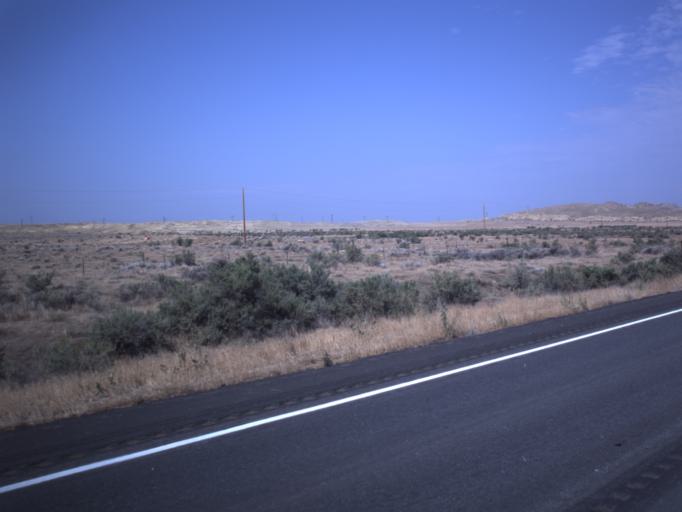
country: US
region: Utah
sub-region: Uintah County
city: Naples
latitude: 40.3106
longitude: -109.2210
